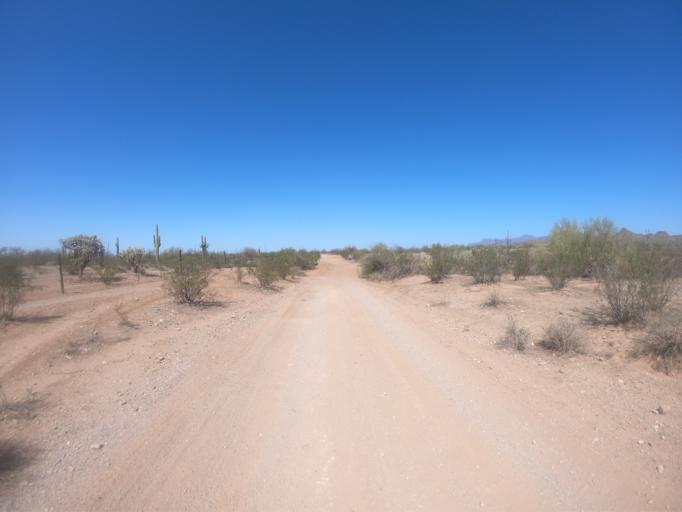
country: US
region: Arizona
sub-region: Pinal County
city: Gold Camp
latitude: 33.2435
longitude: -111.3211
